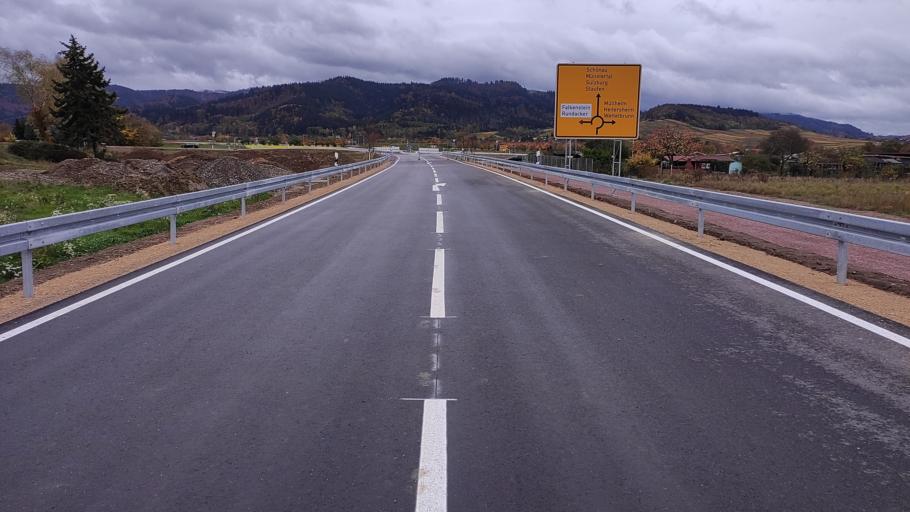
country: DE
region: Baden-Wuerttemberg
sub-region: Freiburg Region
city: Bad Krozingen
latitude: 47.8834
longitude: 7.7147
